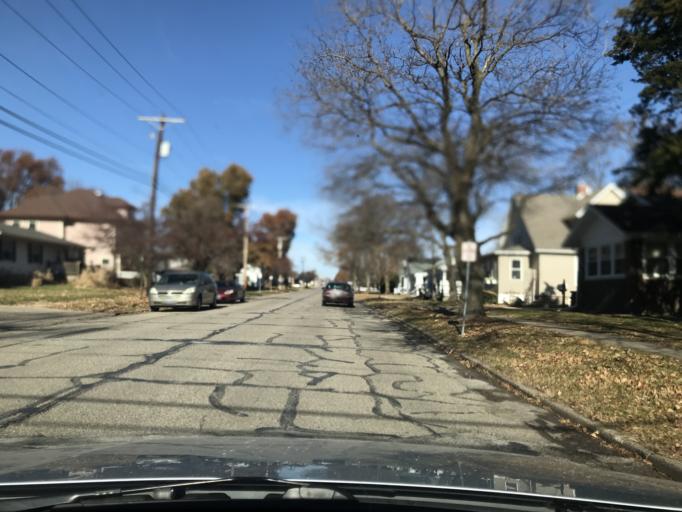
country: US
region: Illinois
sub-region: McDonough County
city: Macomb
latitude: 40.4551
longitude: -90.6672
